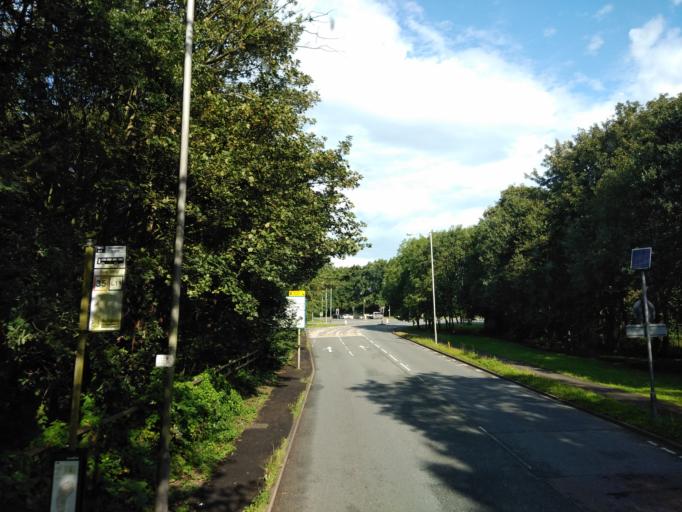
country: GB
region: England
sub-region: Nottinghamshire
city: Kimberley
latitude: 52.9540
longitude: -1.2451
